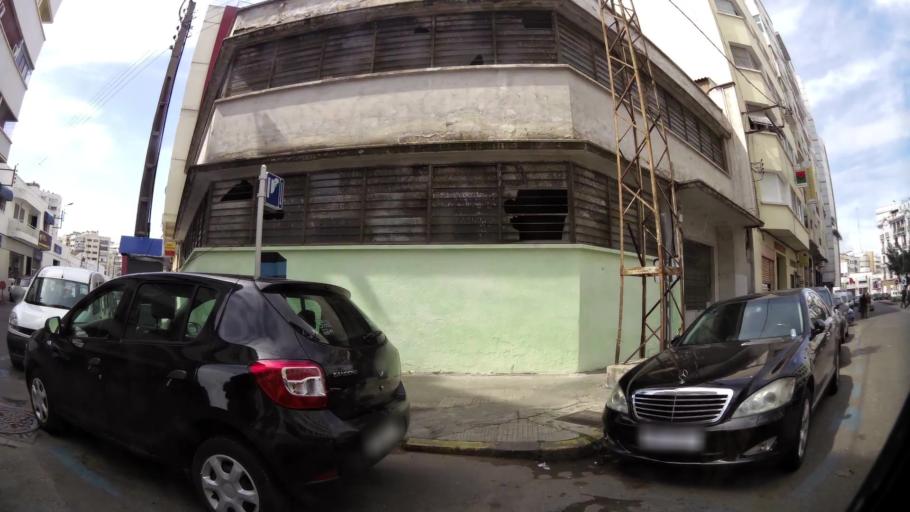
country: MA
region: Grand Casablanca
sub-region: Casablanca
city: Casablanca
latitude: 33.5904
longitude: -7.6020
